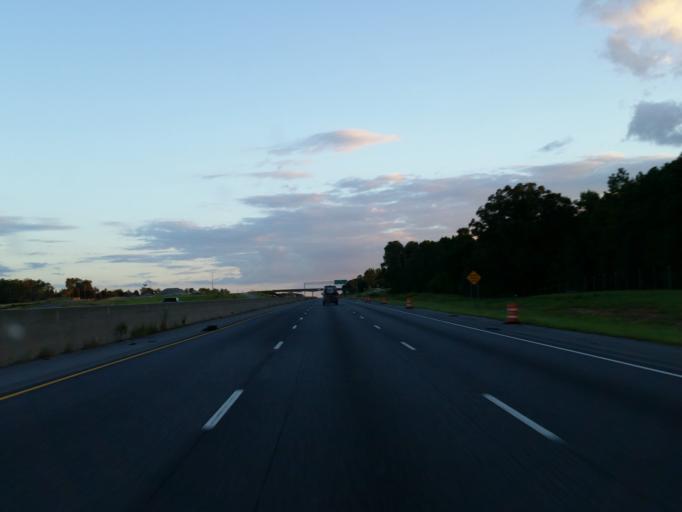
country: US
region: Georgia
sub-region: Tift County
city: Tifton
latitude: 31.5118
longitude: -83.5152
